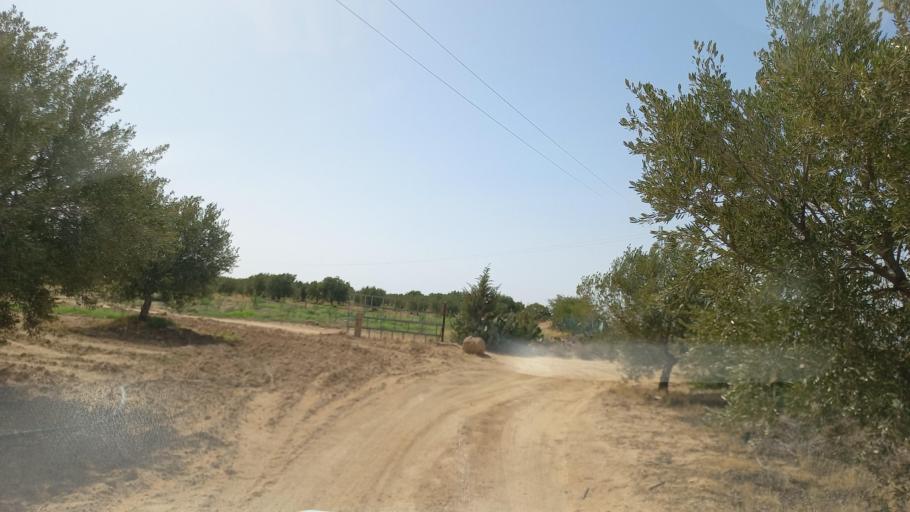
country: TN
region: Al Qasrayn
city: Kasserine
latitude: 35.2136
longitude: 9.0318
